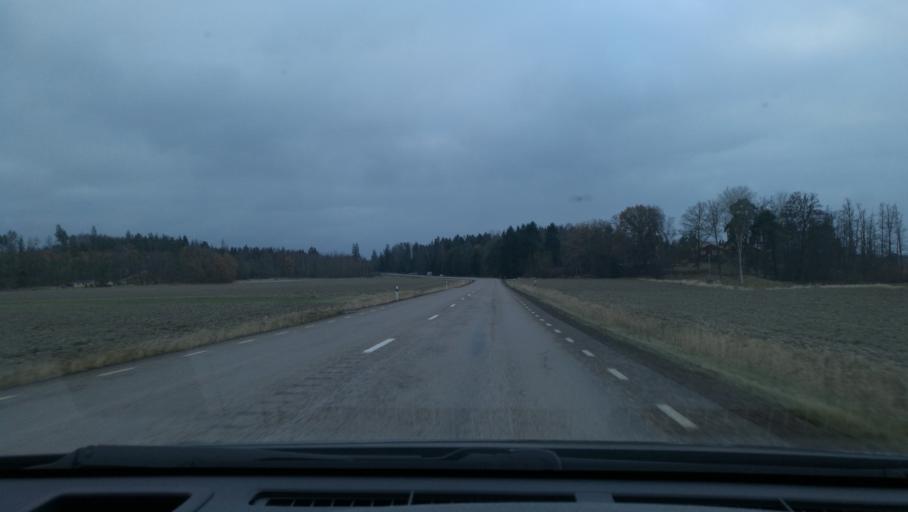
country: SE
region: Vaestmanland
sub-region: Hallstahammars Kommun
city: Kolback
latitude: 59.5386
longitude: 16.3241
